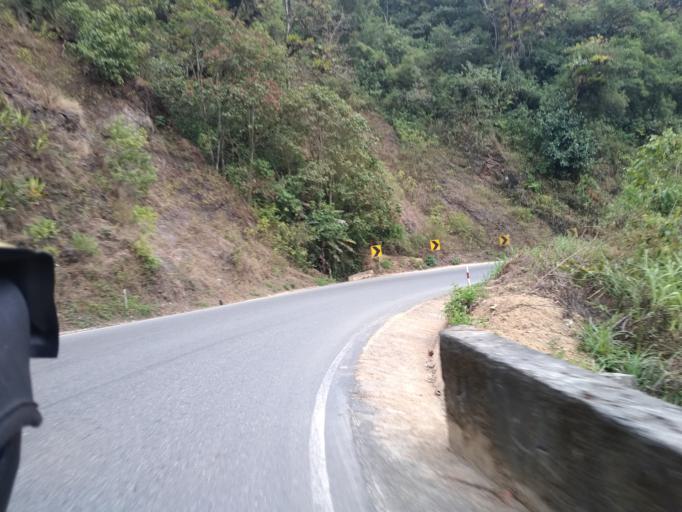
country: EC
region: Cotopaxi
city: La Mana
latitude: -0.8996
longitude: -79.0589
